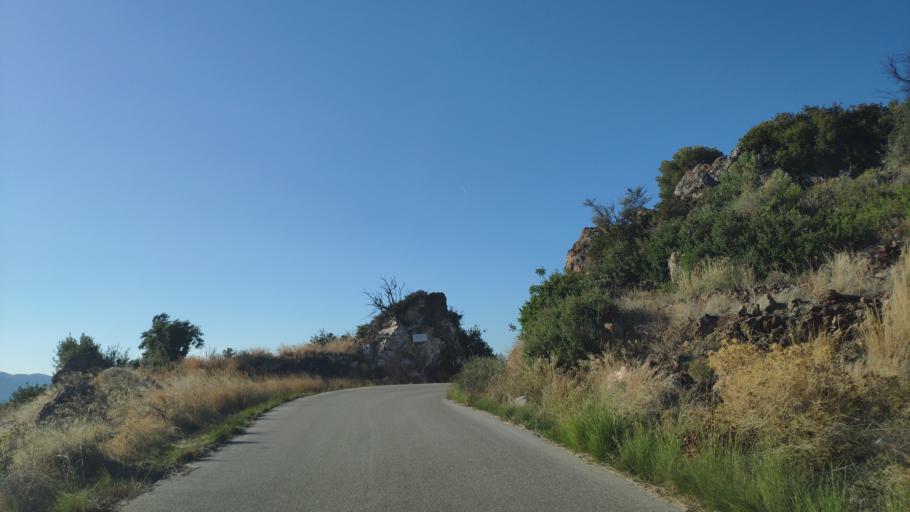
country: GR
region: Attica
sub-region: Nomos Piraios
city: Megalochori
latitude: 37.5812
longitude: 23.3479
